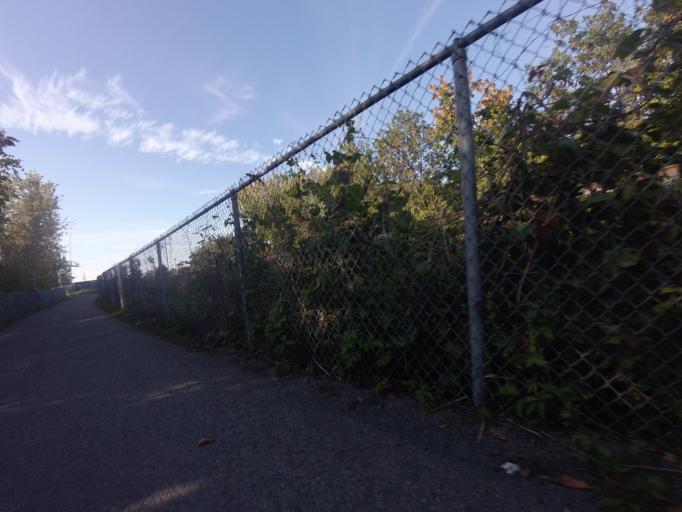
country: CA
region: Quebec
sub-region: Laurentides
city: Saint-Jerome
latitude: 45.7628
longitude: -73.9870
